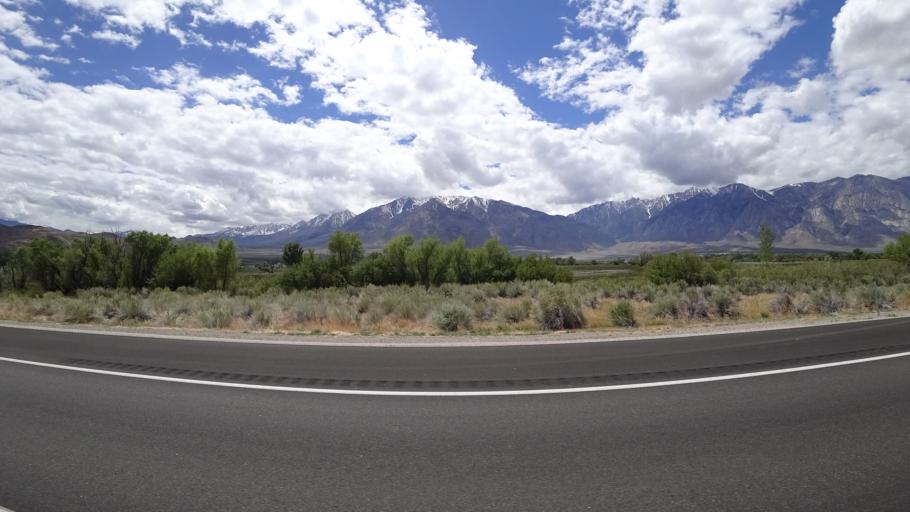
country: US
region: California
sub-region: Inyo County
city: West Bishop
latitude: 37.4112
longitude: -118.5511
